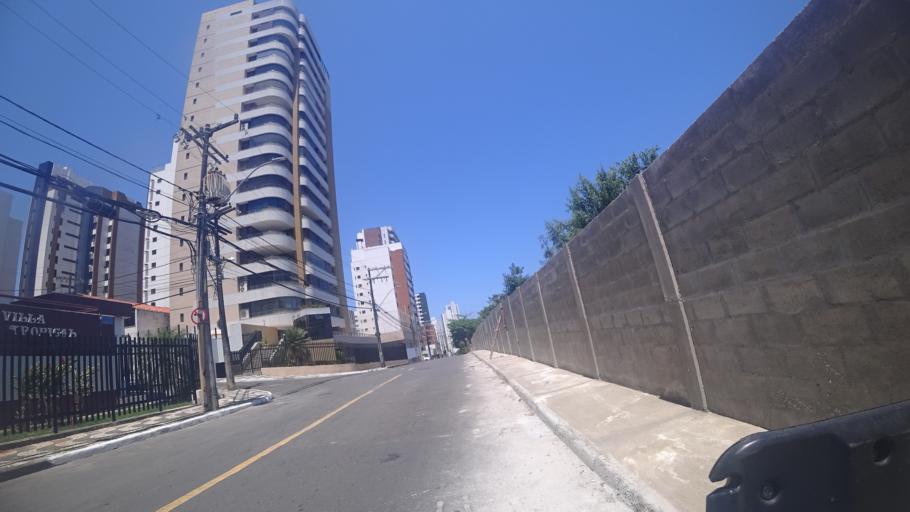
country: BR
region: Bahia
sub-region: Salvador
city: Salvador
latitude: -12.9877
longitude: -38.4608
